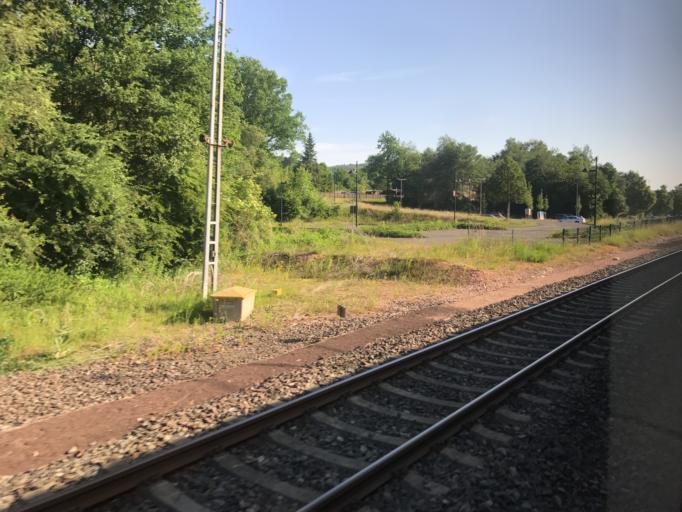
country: DE
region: Rheinland-Pfalz
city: Ellweiler
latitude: 49.6042
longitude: 7.1699
